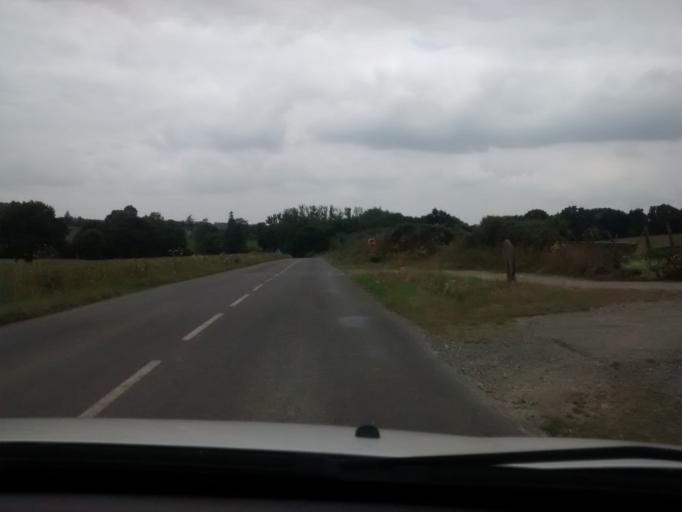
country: FR
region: Brittany
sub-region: Departement d'Ille-et-Vilaine
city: La Bouexiere
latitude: 48.1907
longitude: -1.4486
